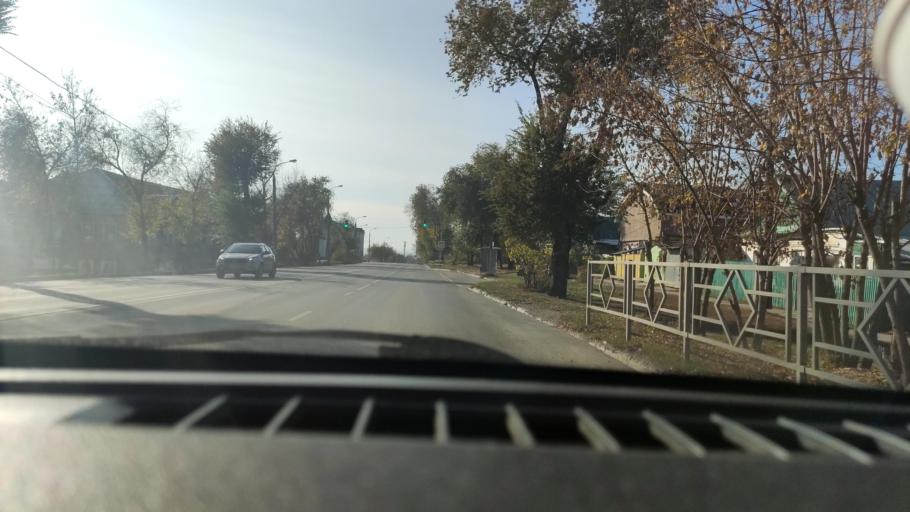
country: RU
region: Samara
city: Samara
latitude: 53.1833
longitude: 50.1998
